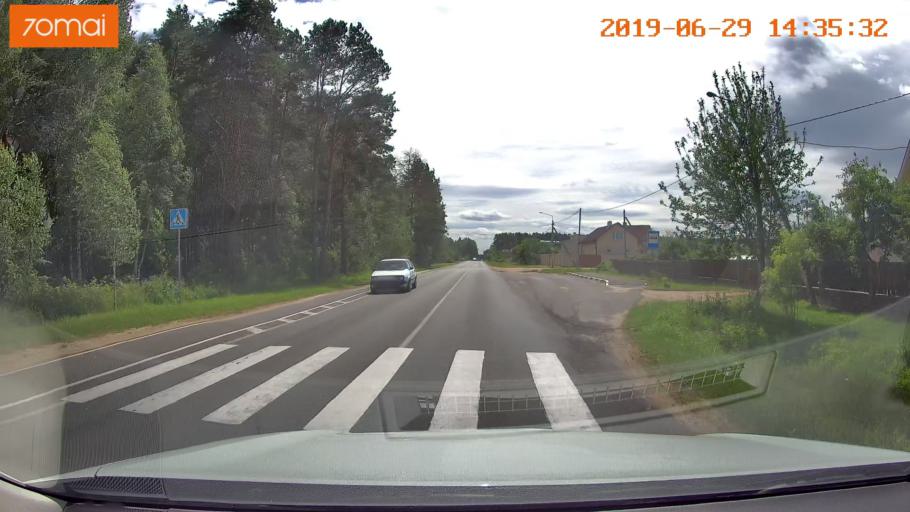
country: BY
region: Minsk
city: Starobin
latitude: 52.7592
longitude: 27.4853
